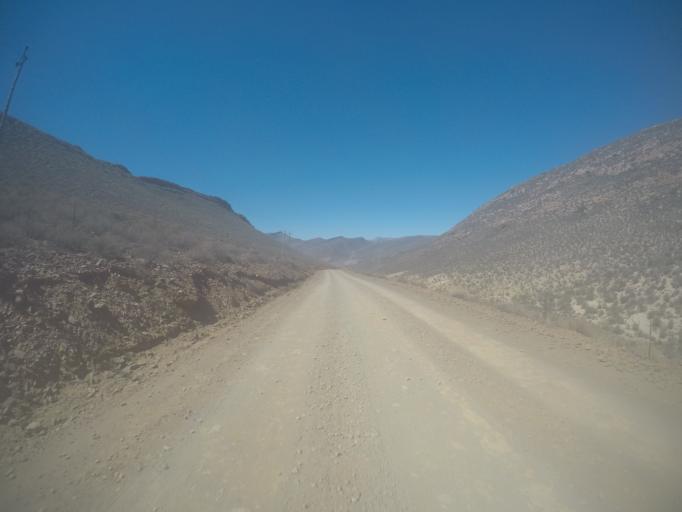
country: ZA
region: Western Cape
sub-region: West Coast District Municipality
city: Clanwilliam
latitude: -32.5350
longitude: 19.3552
